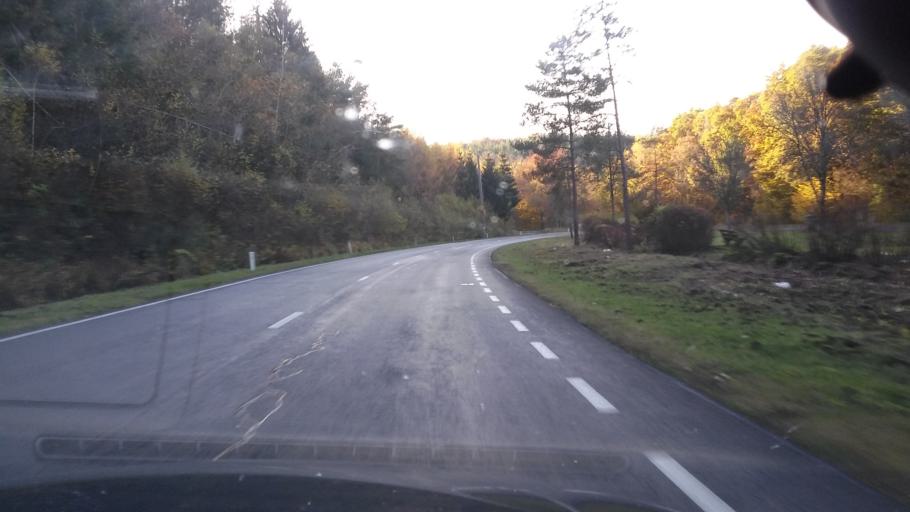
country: BE
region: Wallonia
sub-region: Province du Luxembourg
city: Bouillon
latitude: 49.7598
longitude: 5.1008
